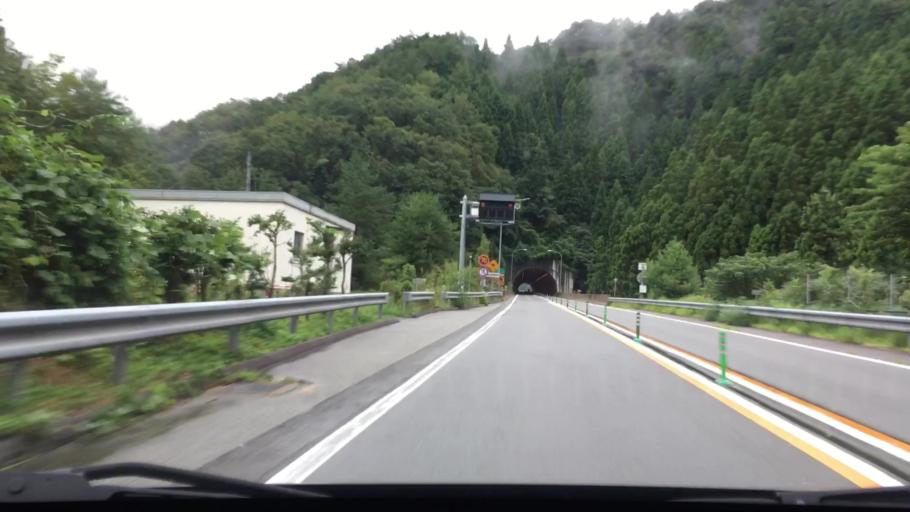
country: JP
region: Hyogo
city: Toyooka
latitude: 35.2567
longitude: 134.7944
